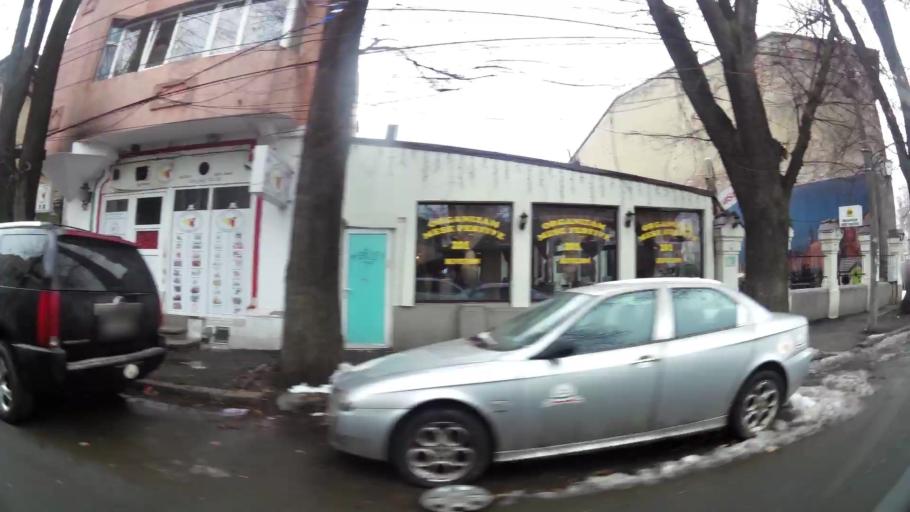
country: RO
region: Bucuresti
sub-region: Municipiul Bucuresti
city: Bucharest
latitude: 44.4411
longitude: 26.1284
